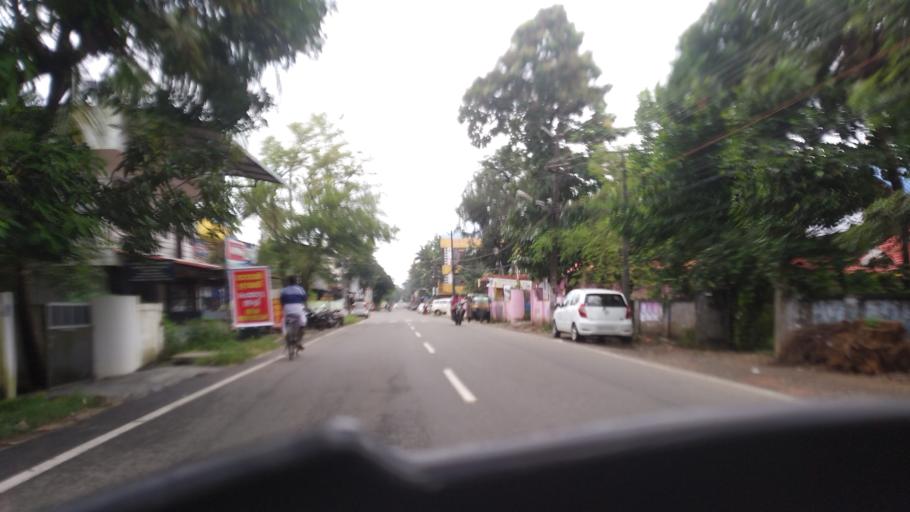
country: IN
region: Kerala
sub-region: Ernakulam
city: Elur
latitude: 10.0949
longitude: 76.2066
